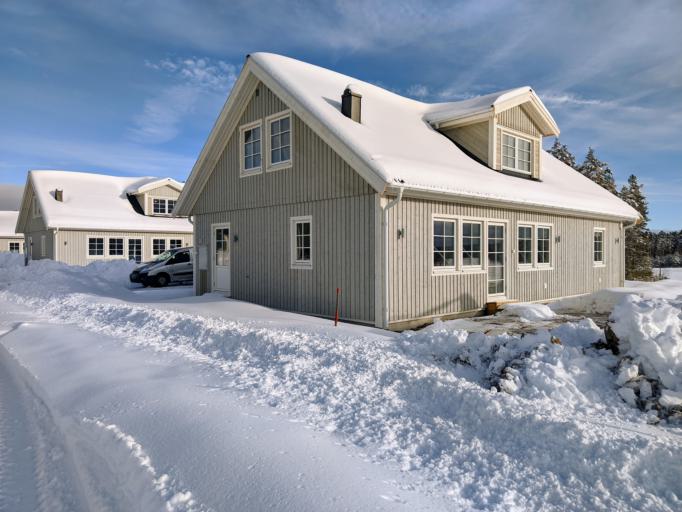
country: NO
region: Hedmark
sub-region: Elverum
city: Elverum
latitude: 60.8999
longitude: 11.5191
